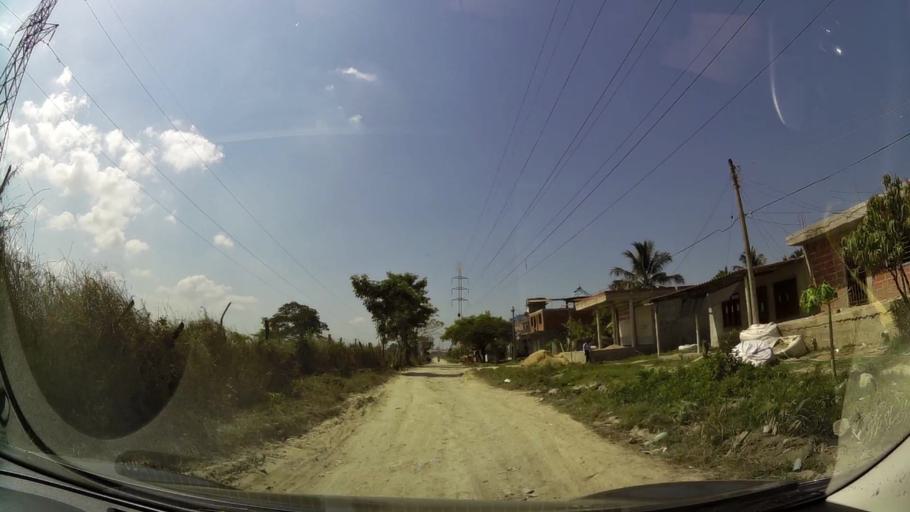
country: CO
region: Bolivar
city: Cartagena
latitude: 10.3550
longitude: -75.4834
